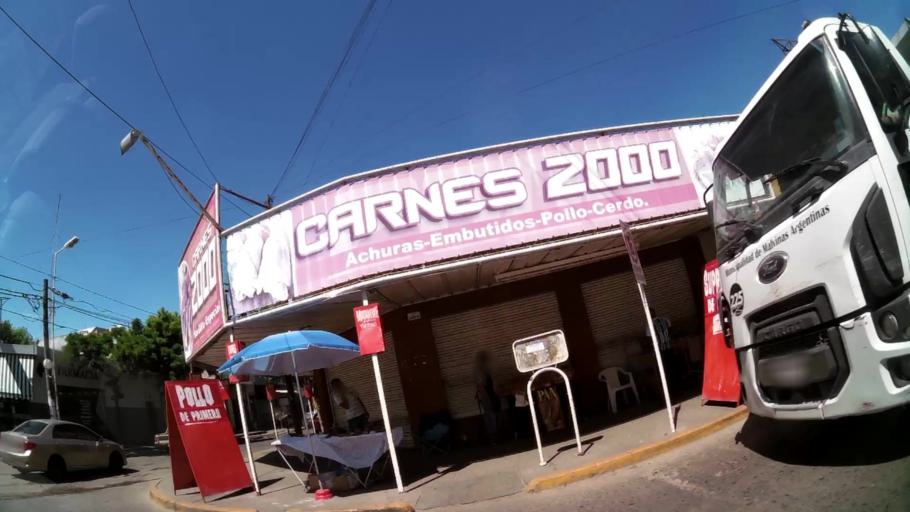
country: AR
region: Buenos Aires
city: Hurlingham
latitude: -34.5025
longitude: -58.6673
